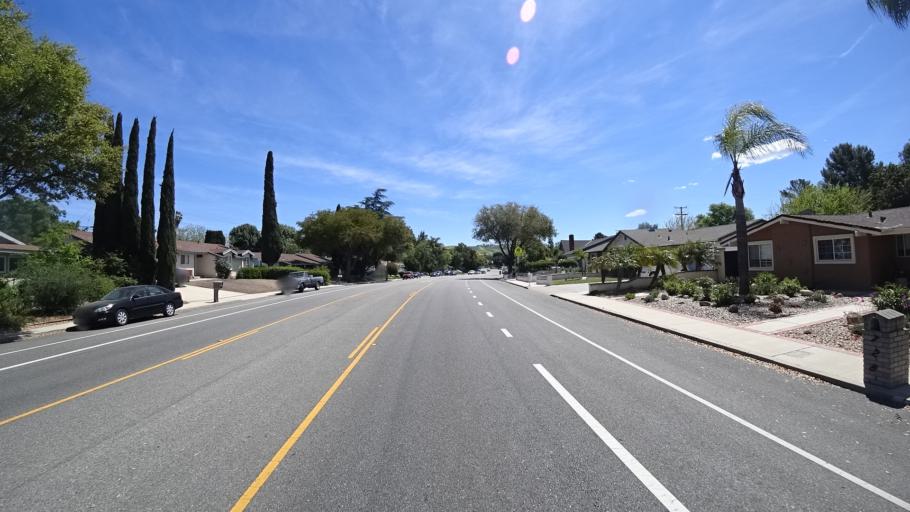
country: US
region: California
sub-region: Ventura County
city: Thousand Oaks
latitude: 34.2176
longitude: -118.8654
